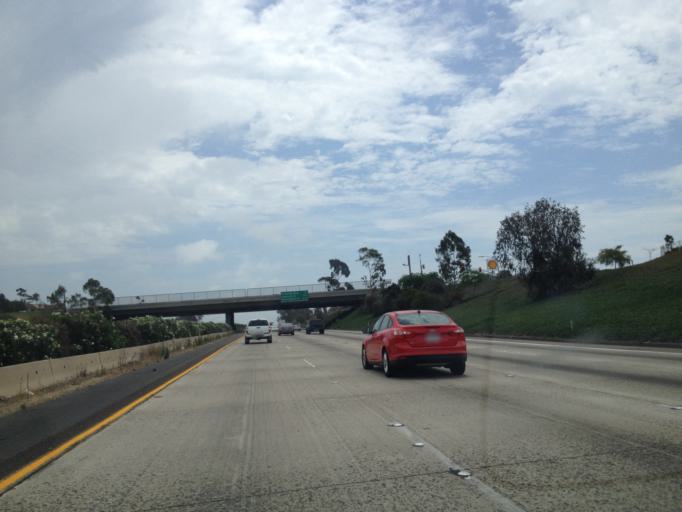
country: US
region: California
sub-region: San Diego County
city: Encinitas
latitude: 33.0668
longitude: -117.2928
